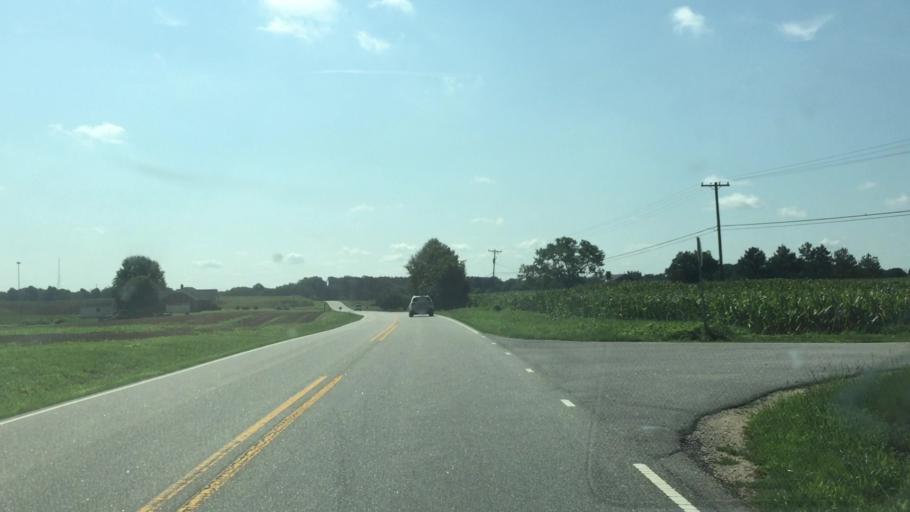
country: US
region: North Carolina
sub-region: Stanly County
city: Oakboro
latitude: 35.1276
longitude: -80.3621
